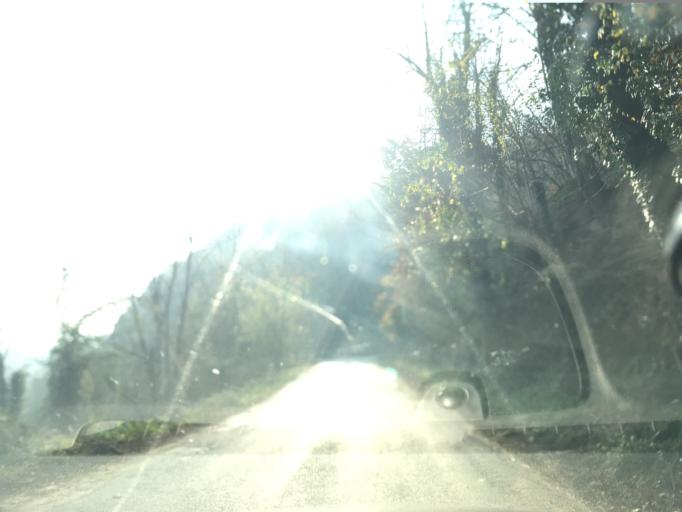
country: TR
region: Duzce
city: Cumayeri
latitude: 40.9158
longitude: 30.9353
